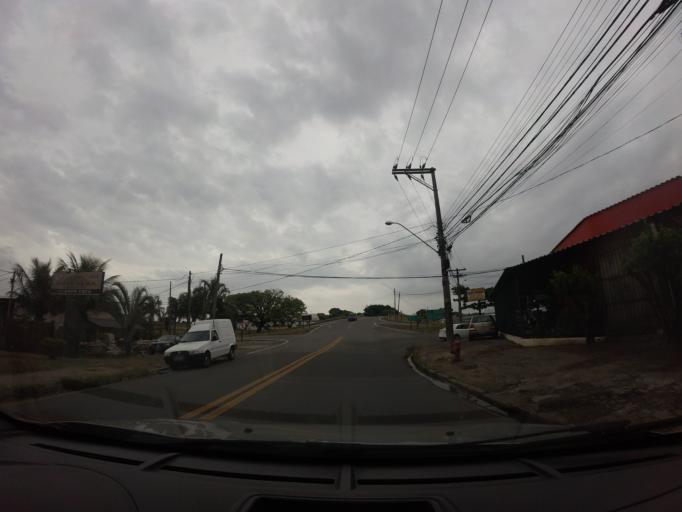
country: BR
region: Sao Paulo
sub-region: Piracicaba
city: Piracicaba
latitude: -22.7425
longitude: -47.5992
